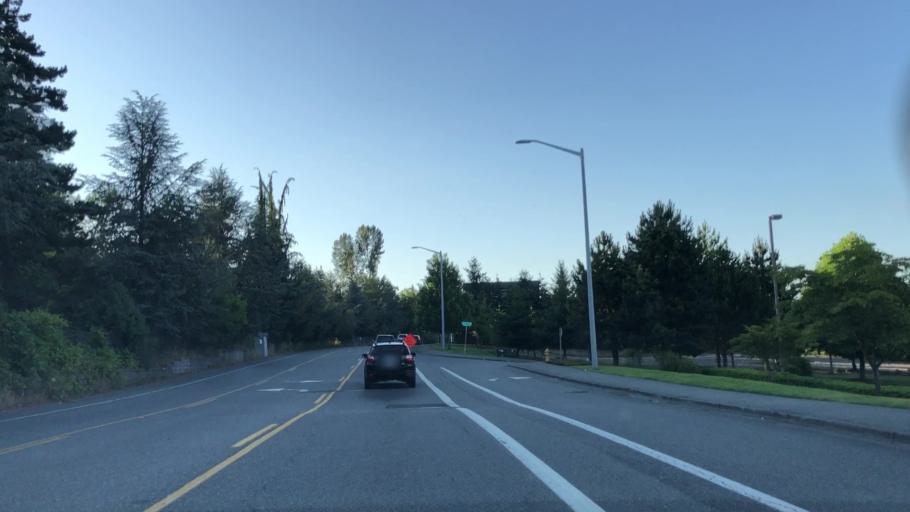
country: US
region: Washington
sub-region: Snohomish County
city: Alderwood Manor
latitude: 47.8512
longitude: -122.2716
